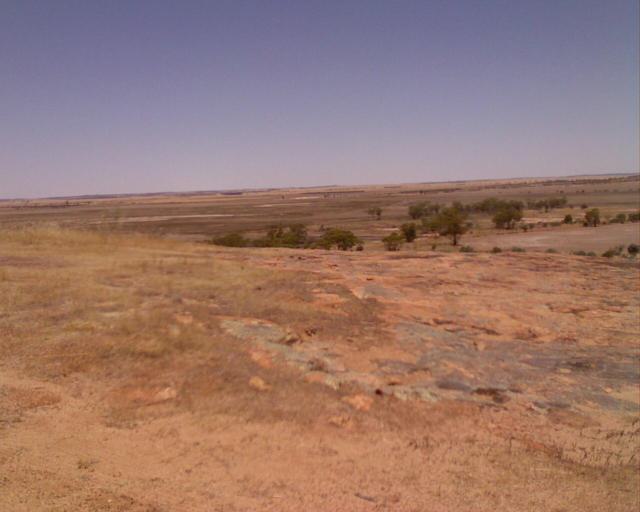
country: AU
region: Western Australia
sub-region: Merredin
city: Merredin
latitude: -30.8419
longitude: 117.9047
